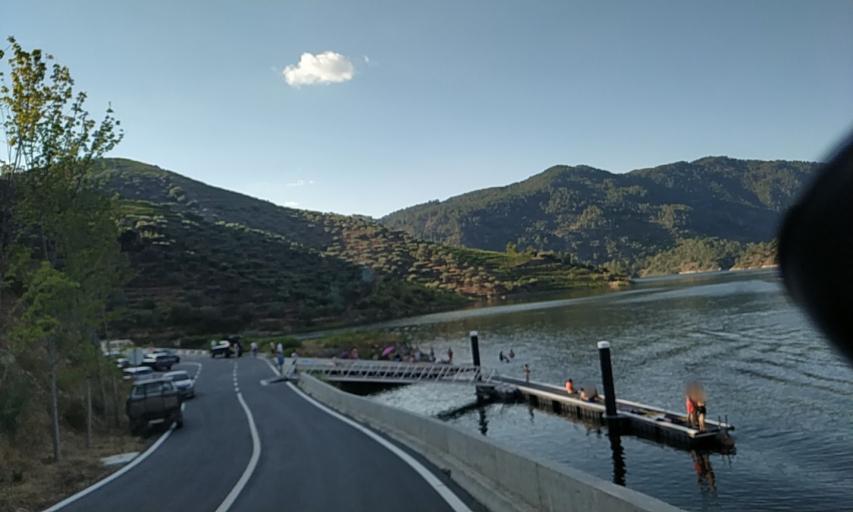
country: PT
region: Viseu
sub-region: Sao Joao da Pesqueira
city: Sao Joao da Pesqueira
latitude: 41.2316
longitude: -7.4247
